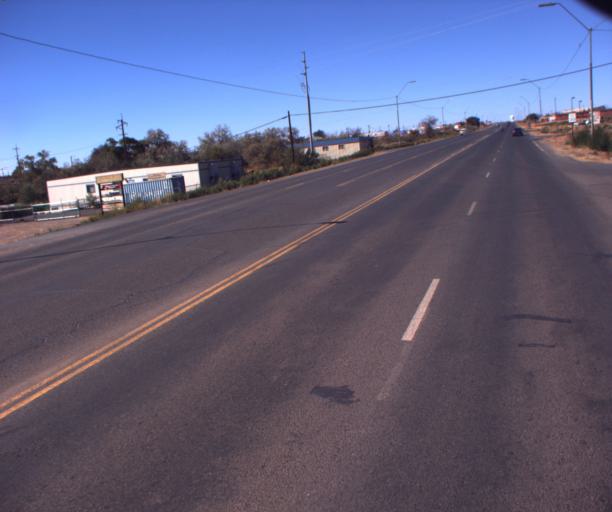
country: US
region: Arizona
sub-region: Coconino County
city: Tuba City
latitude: 36.1199
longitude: -111.2298
